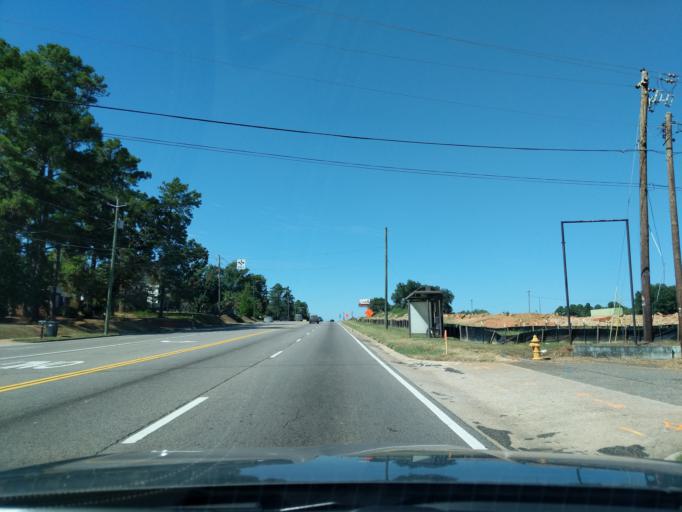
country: US
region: South Carolina
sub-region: Aiken County
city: North Augusta
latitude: 33.4999
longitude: -82.0122
